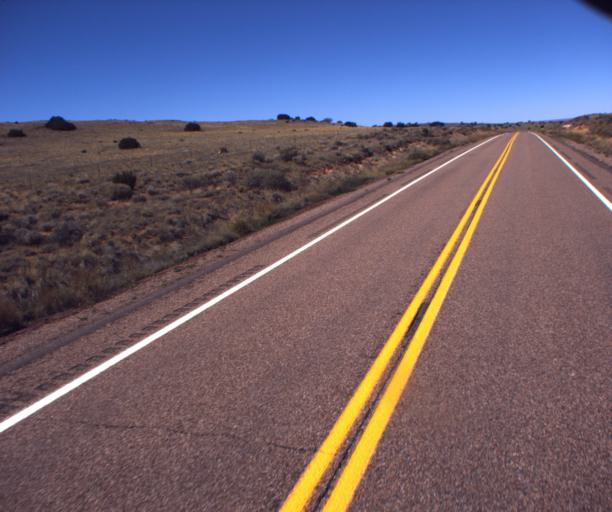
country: US
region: Arizona
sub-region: Apache County
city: Saint Johns
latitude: 34.5597
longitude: -109.4999
